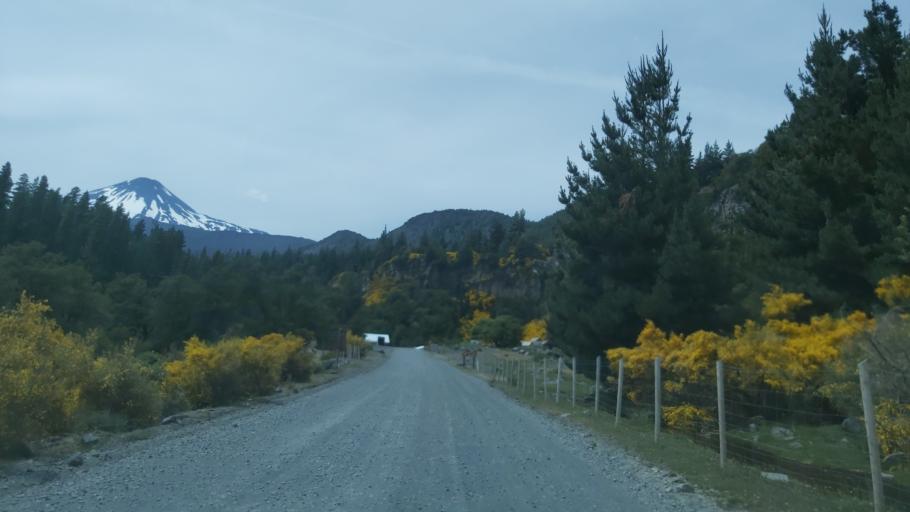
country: AR
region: Neuquen
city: Las Ovejas
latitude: -37.3952
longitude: -71.4582
